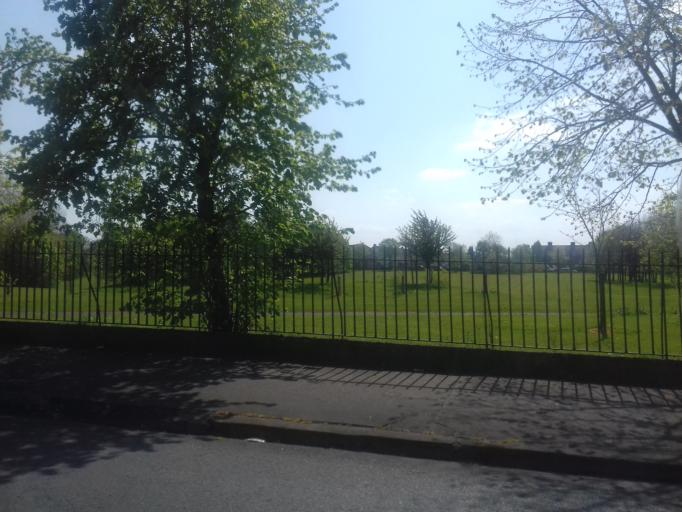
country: IE
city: Bonnybrook
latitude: 53.3975
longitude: -6.2067
